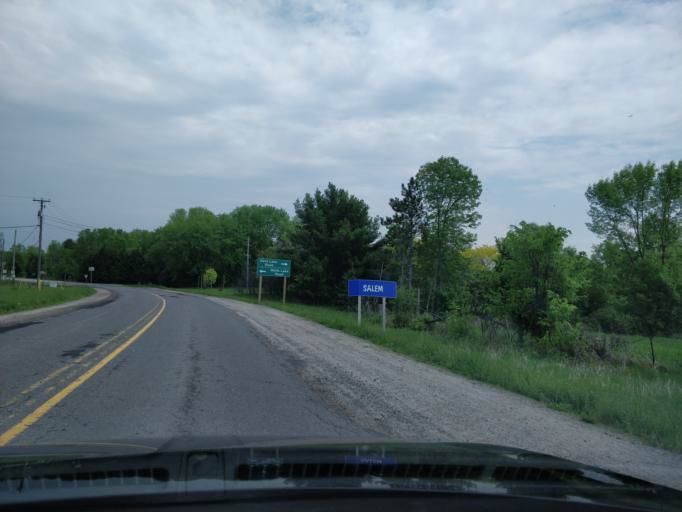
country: CA
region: Ontario
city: Perth
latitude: 44.6552
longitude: -76.4559
